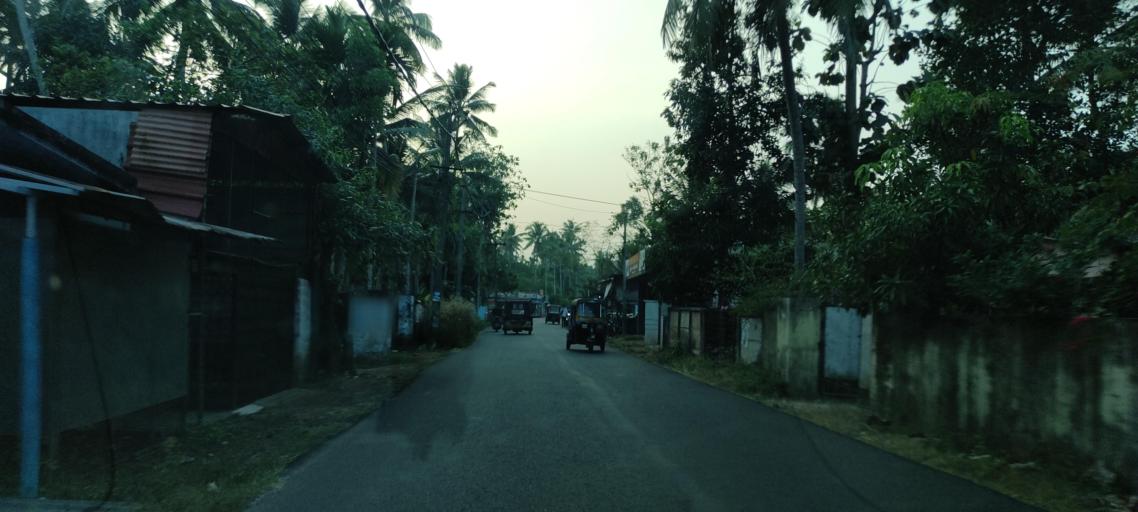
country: IN
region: Kerala
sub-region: Alappuzha
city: Kayankulam
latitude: 9.1376
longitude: 76.5171
